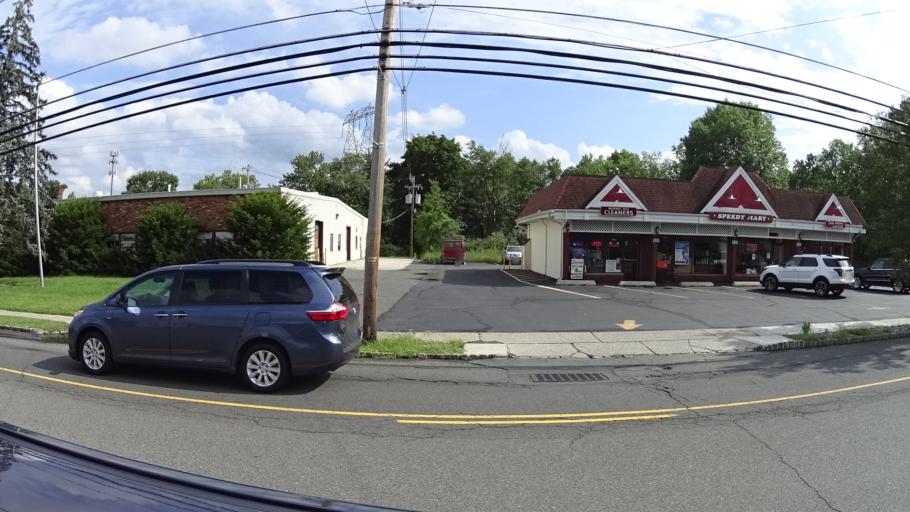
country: US
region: New Jersey
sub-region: Somerset County
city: Watchung
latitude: 40.6679
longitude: -74.4929
